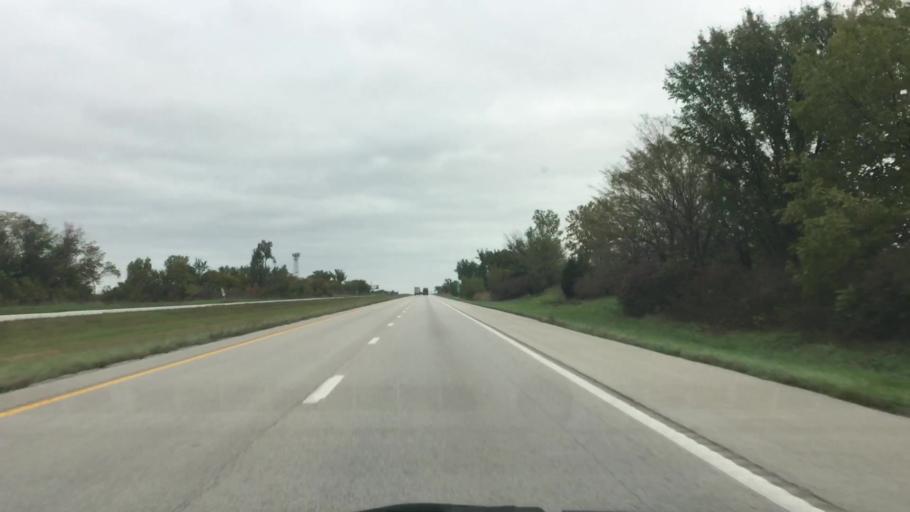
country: US
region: Missouri
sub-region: Clinton County
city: Cameron
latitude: 39.8235
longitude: -94.1899
